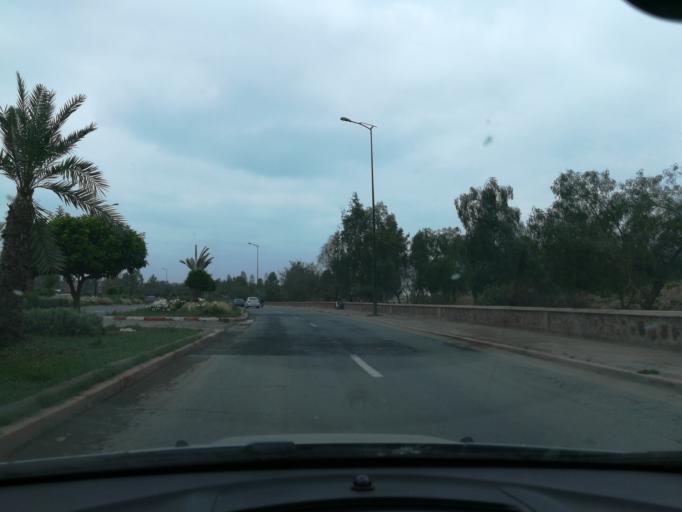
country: MA
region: Marrakech-Tensift-Al Haouz
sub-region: Marrakech
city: Marrakesh
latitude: 31.6583
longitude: -7.9844
